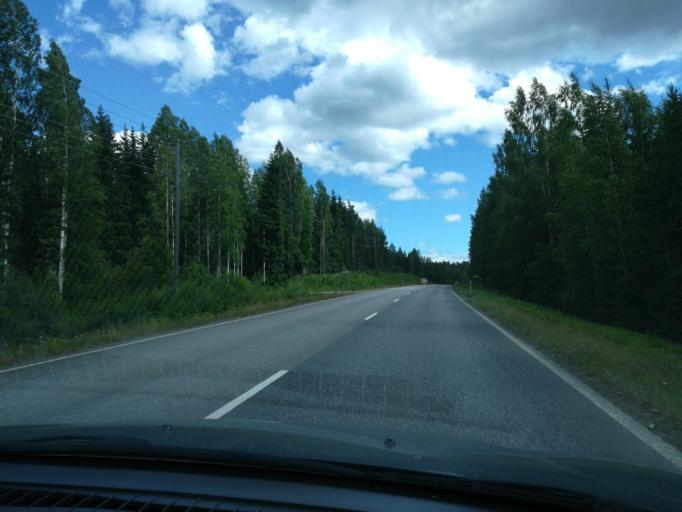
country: FI
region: Southern Savonia
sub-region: Mikkeli
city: Hirvensalmi
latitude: 61.6704
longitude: 26.7951
